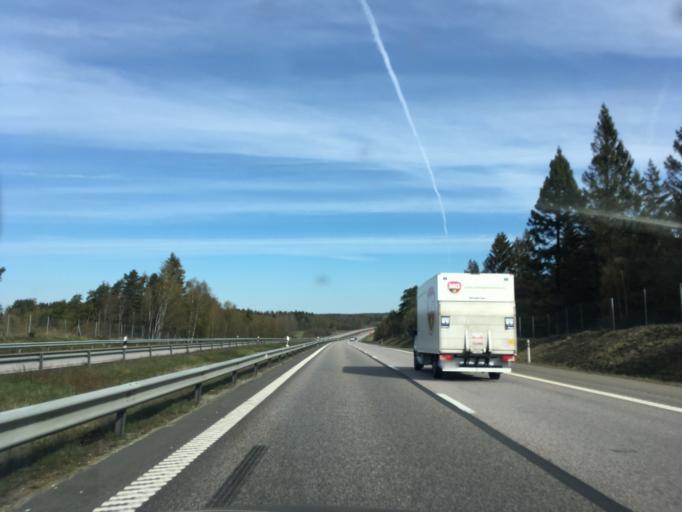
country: SE
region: Halland
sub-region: Varbergs Kommun
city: Veddige
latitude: 57.2018
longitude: 12.2482
